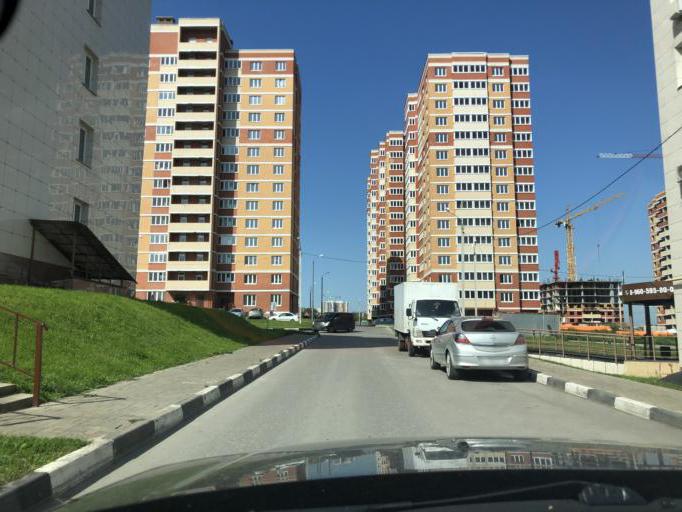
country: RU
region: Tula
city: Tula
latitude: 54.1747
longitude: 37.6551
